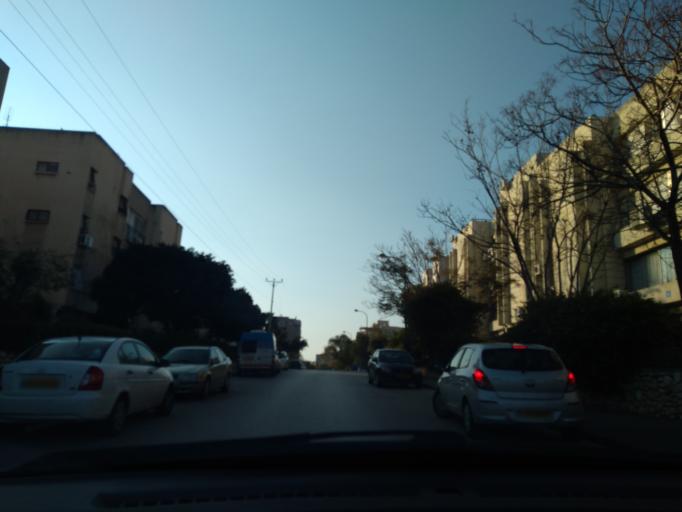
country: IL
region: Central District
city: Even Yehuda
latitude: 32.2818
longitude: 34.8563
